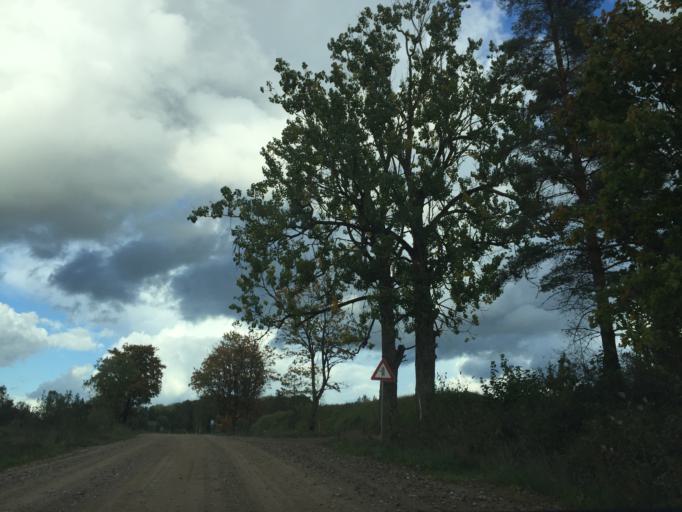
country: LV
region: Amatas Novads
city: Drabesi
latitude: 57.0635
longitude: 25.1773
